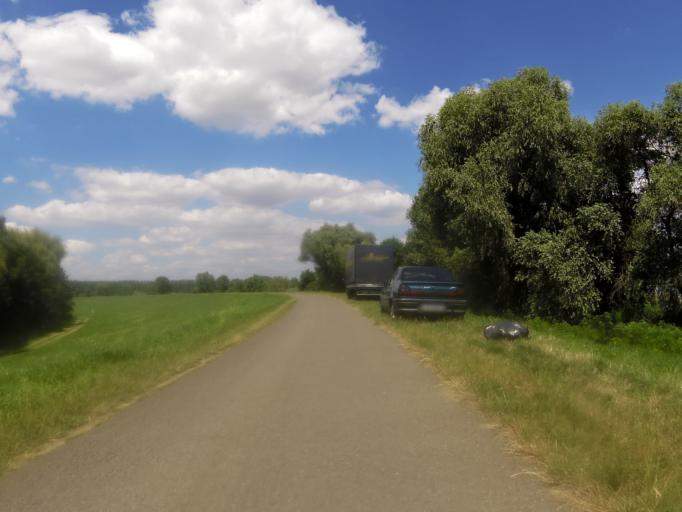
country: HU
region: Heves
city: Tiszanana
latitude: 47.5661
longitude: 20.6108
